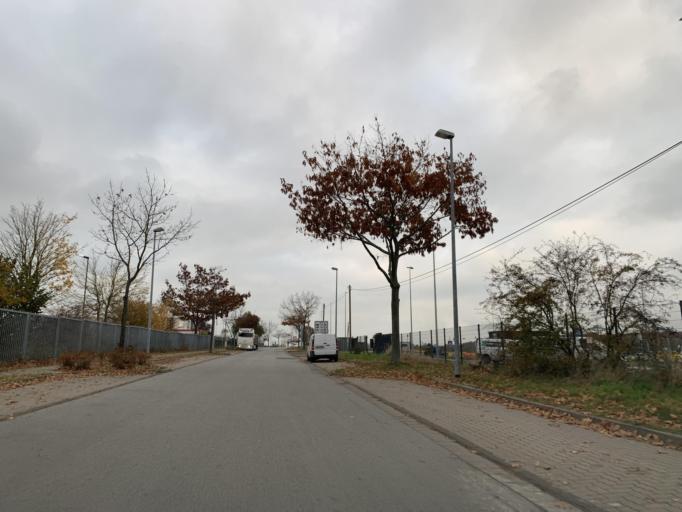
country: DE
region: Mecklenburg-Vorpommern
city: Trollenhagen
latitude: 53.5835
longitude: 13.2899
